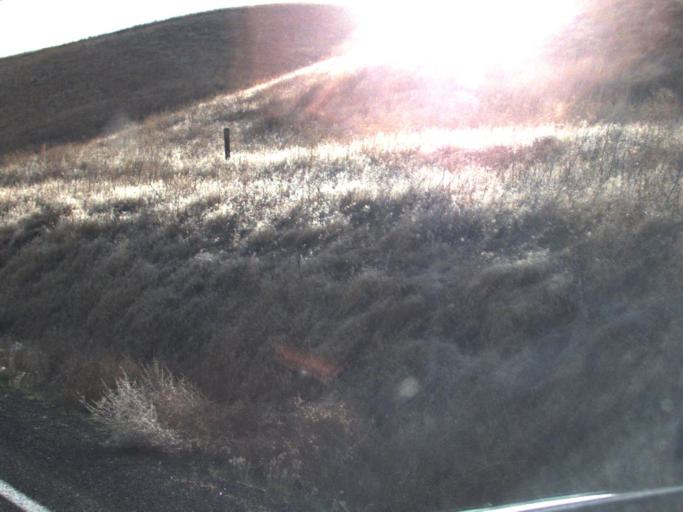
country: US
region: Washington
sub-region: Columbia County
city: Dayton
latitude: 46.4631
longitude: -117.9613
